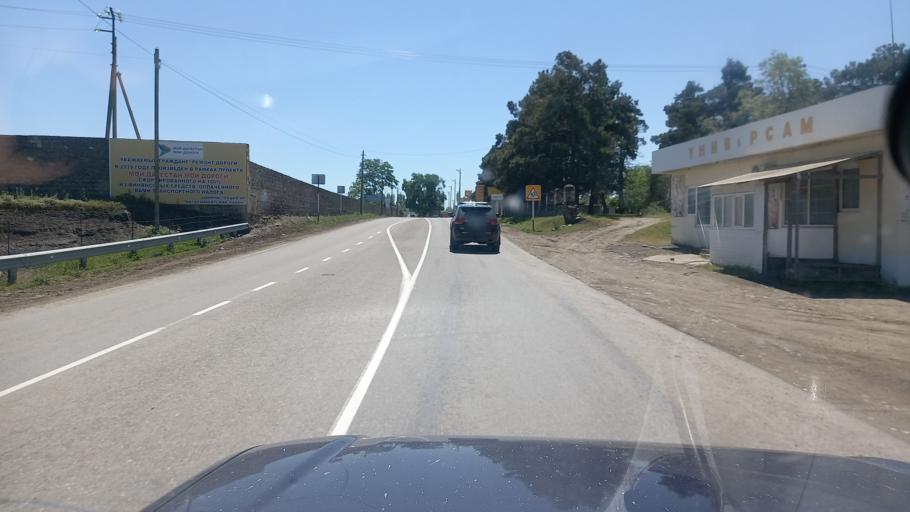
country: AZ
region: Qusar
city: Samur
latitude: 41.7273
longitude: 48.4557
